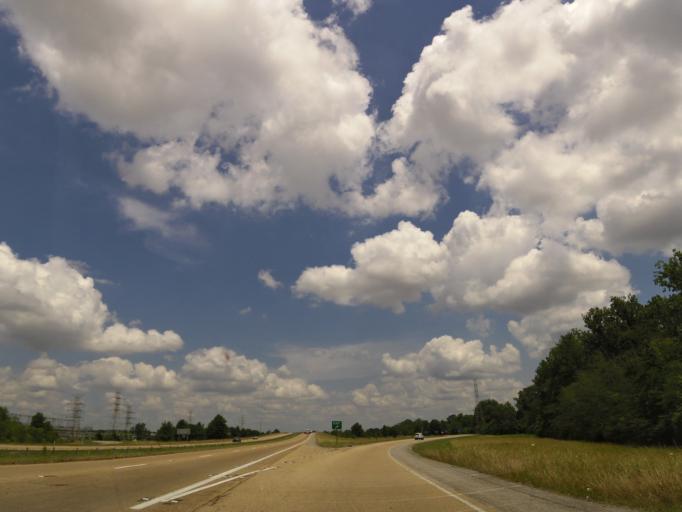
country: US
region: Mississippi
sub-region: Lee County
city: Tupelo
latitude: 34.2523
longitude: -88.6938
